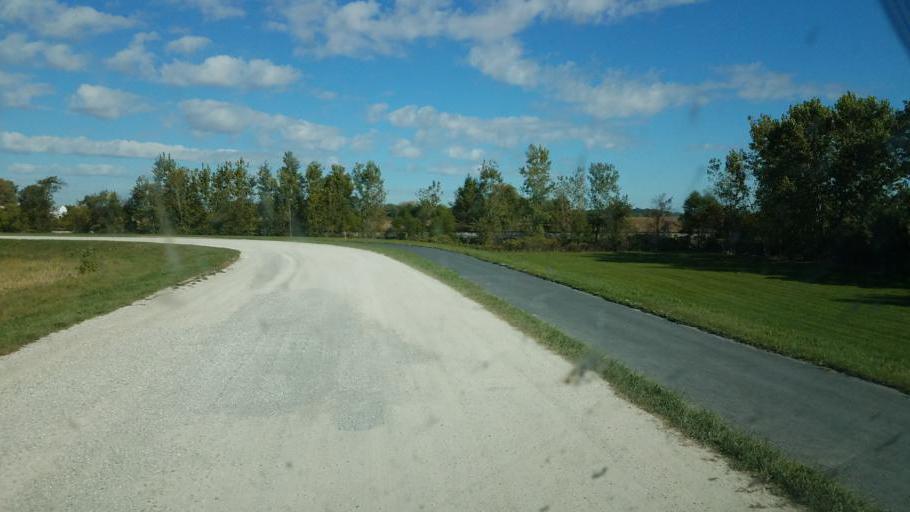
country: US
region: Ohio
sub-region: Wyandot County
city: Upper Sandusky
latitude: 40.8226
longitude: -83.2480
